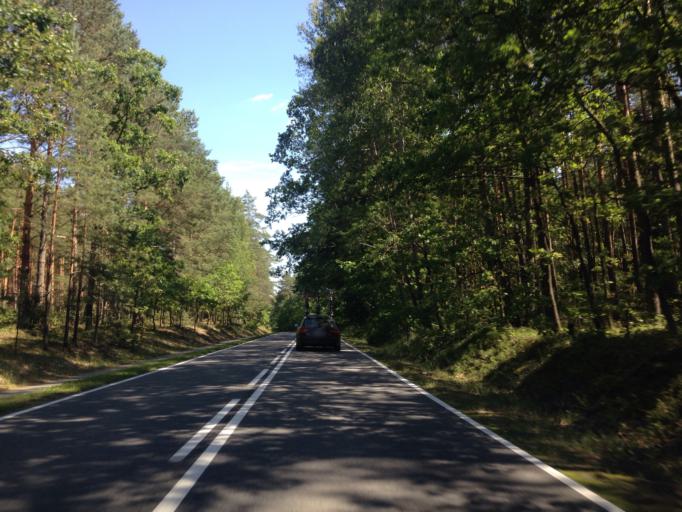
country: PL
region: Kujawsko-Pomorskie
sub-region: Powiat swiecki
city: Osie
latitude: 53.6107
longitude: 18.2997
